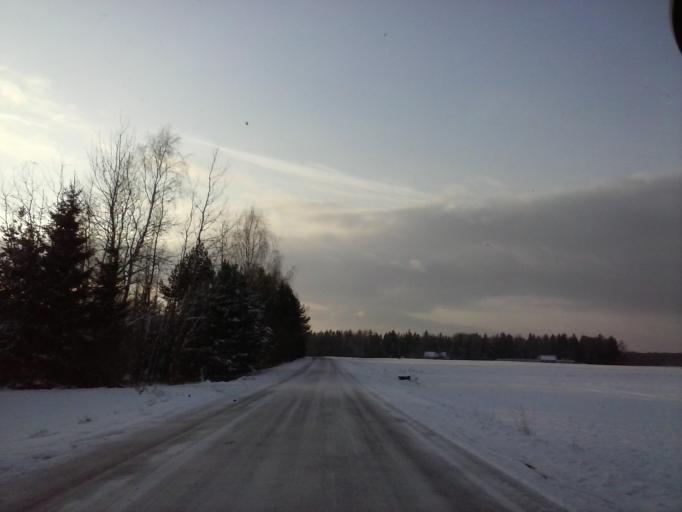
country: EE
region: Tartu
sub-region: UElenurme vald
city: Ulenurme
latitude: 58.3214
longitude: 26.8779
